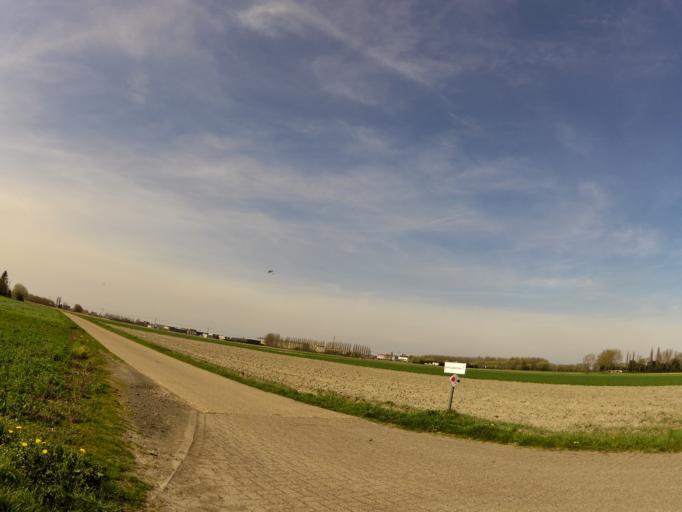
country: BE
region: Flanders
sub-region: Provincie West-Vlaanderen
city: Oudenburg
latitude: 51.1920
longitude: 3.0207
